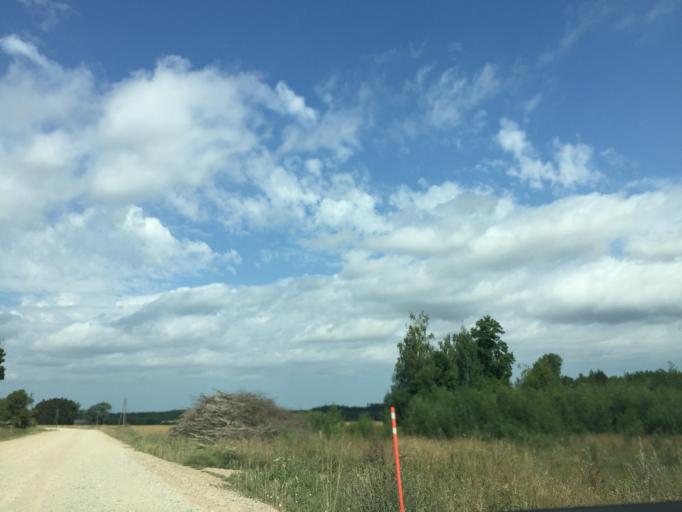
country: LV
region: Kandava
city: Kandava
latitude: 56.9955
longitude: 22.8905
